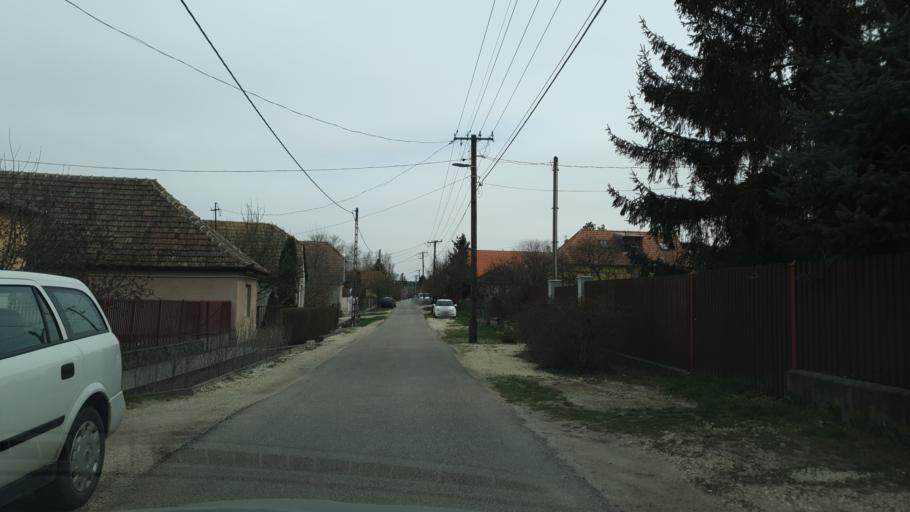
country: HU
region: Fejer
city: Etyek
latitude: 47.4459
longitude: 18.7464
